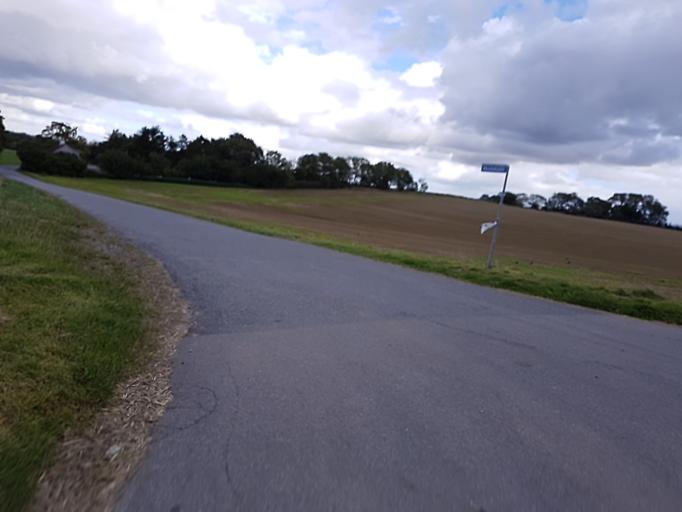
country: DK
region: Zealand
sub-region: Roskilde Kommune
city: Gundsomagle
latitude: 55.7152
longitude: 12.1452
